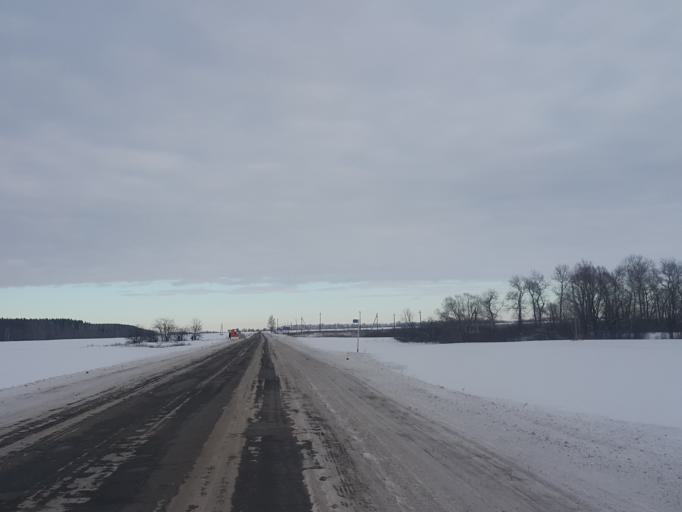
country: RU
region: Tambov
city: Novaya Lyada
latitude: 52.7511
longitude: 41.7153
